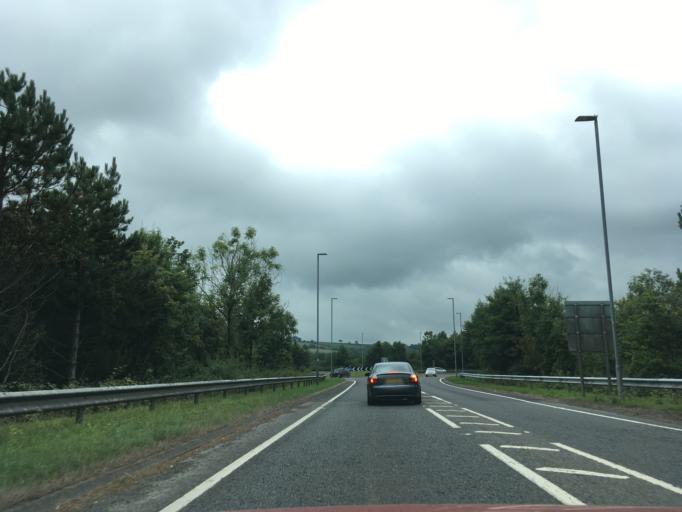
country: GB
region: Wales
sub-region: Carmarthenshire
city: Whitland
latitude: 51.8221
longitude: -4.6245
